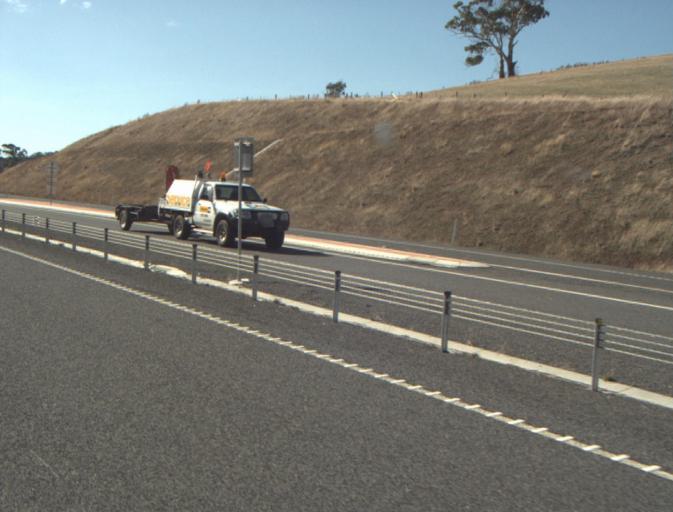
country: AU
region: Tasmania
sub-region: Launceston
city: Mayfield
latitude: -41.3564
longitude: 147.1051
